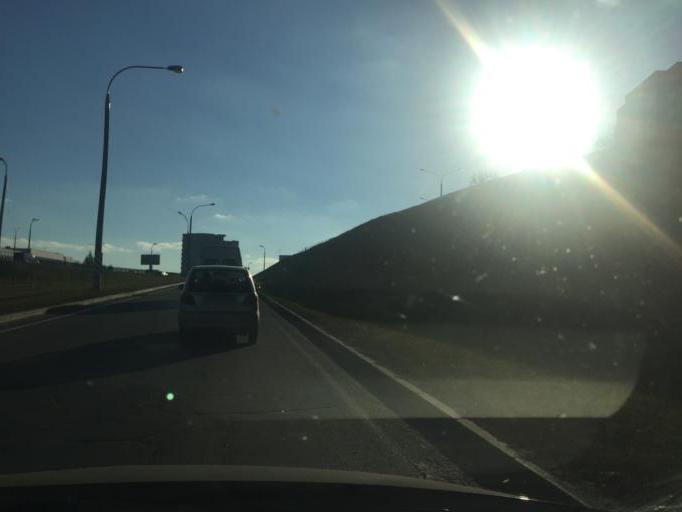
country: BY
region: Minsk
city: Vyaliki Trastsyanets
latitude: 53.8685
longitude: 27.6892
